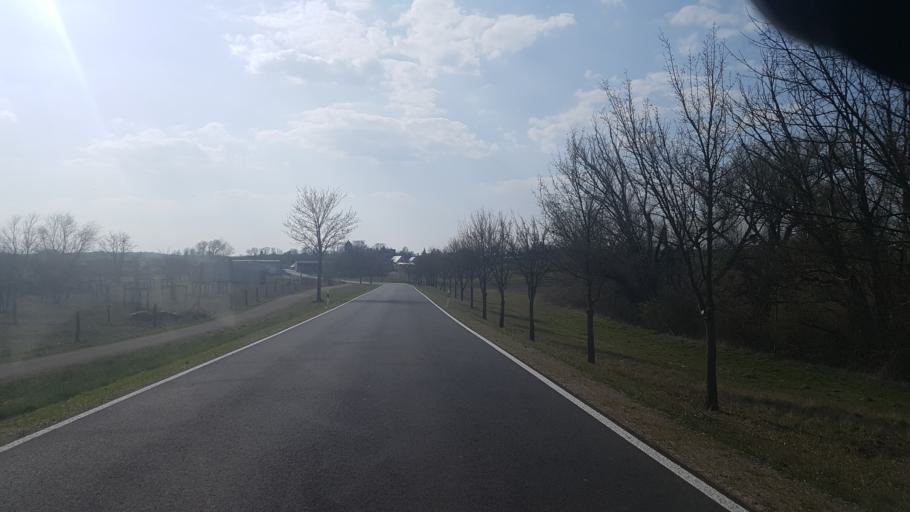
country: DE
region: Brandenburg
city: Gerswalde
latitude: 53.1747
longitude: 13.7843
